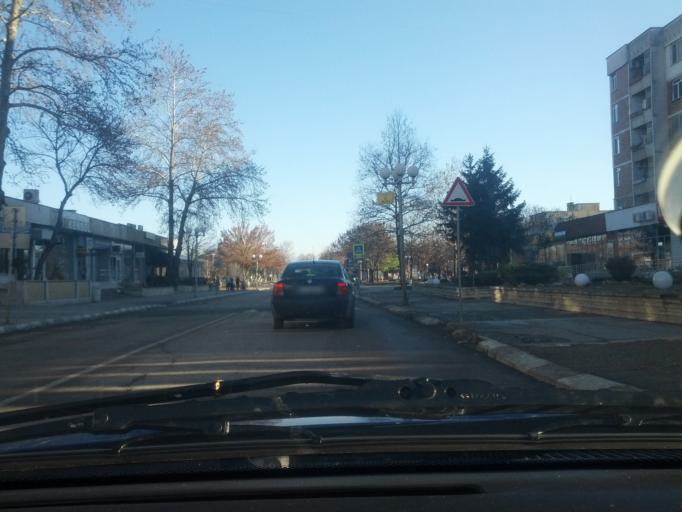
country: BG
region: Vratsa
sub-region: Obshtina Kozloduy
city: Kozloduy
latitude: 43.7783
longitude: 23.7278
